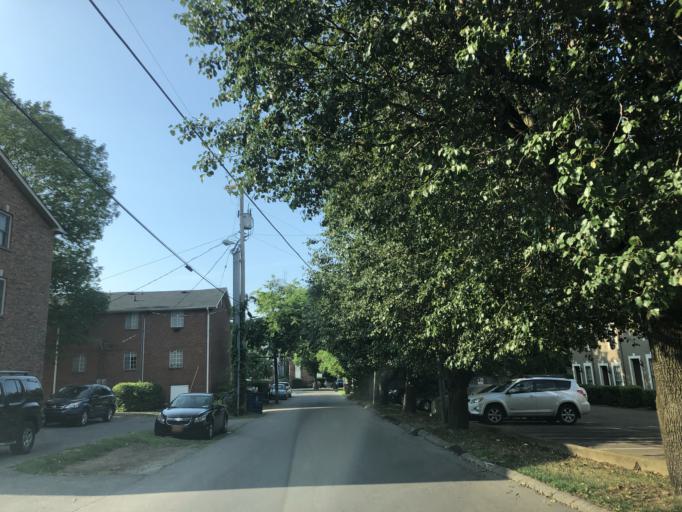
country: US
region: Tennessee
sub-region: Davidson County
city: Nashville
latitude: 36.1334
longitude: -86.8029
